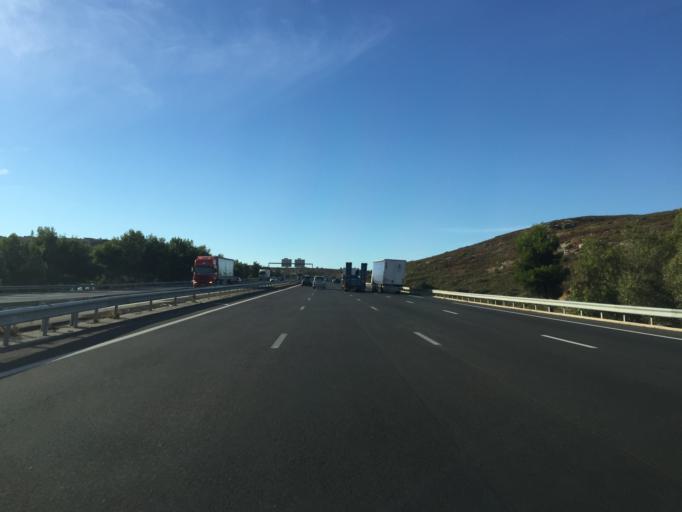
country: FR
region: Provence-Alpes-Cote d'Azur
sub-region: Departement des Bouches-du-Rhone
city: Coudoux
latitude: 43.5681
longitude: 5.2219
